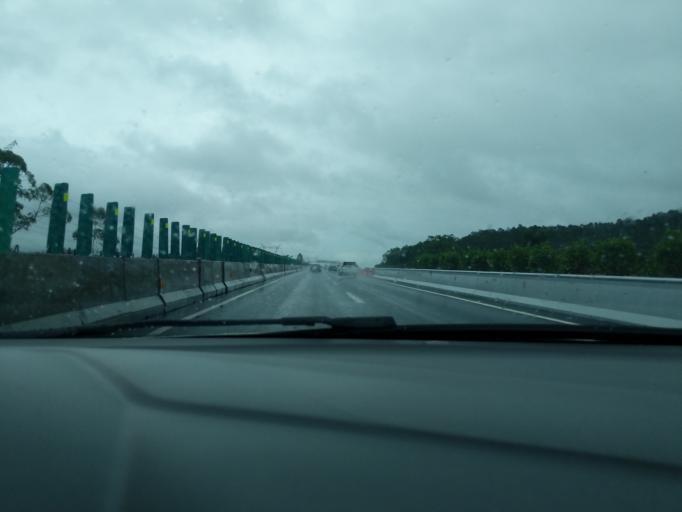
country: CN
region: Guangdong
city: Pingshi
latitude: 22.2563
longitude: 112.3110
